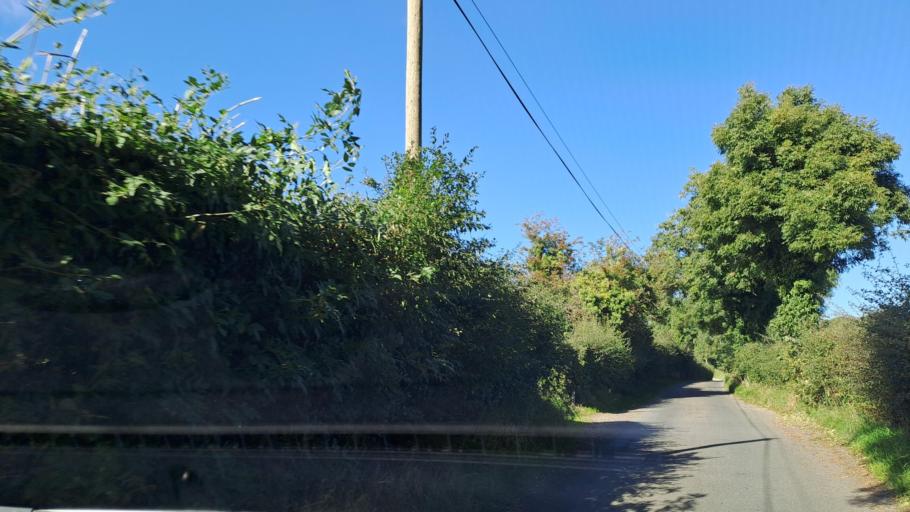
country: IE
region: Ulster
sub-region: County Monaghan
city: Carrickmacross
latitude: 53.9913
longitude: -6.7552
